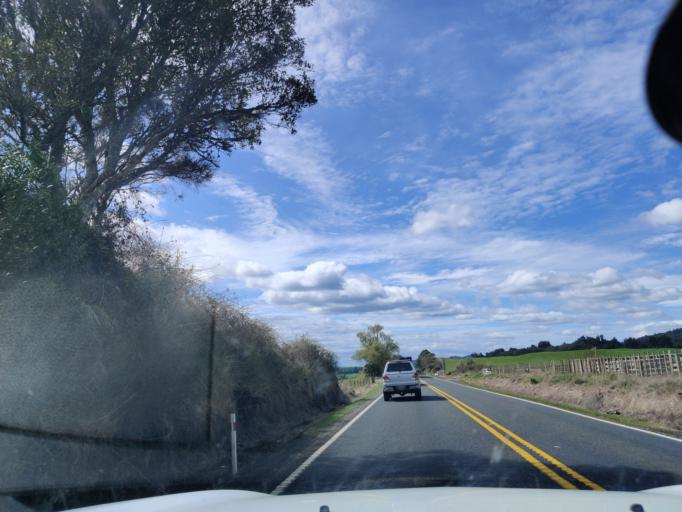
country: NZ
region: Waikato
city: Turangi
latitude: -39.0636
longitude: 175.3718
